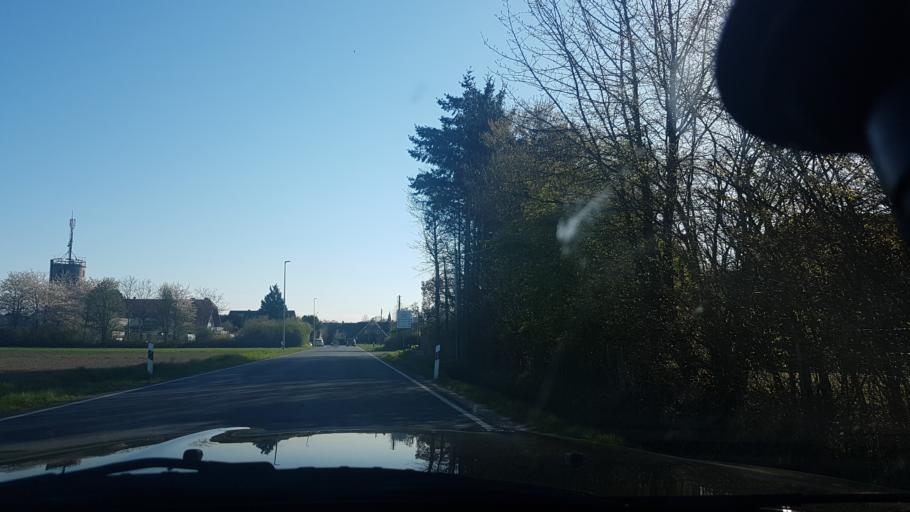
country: DE
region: Lower Saxony
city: Hemmingen
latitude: 52.2775
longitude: 9.7035
